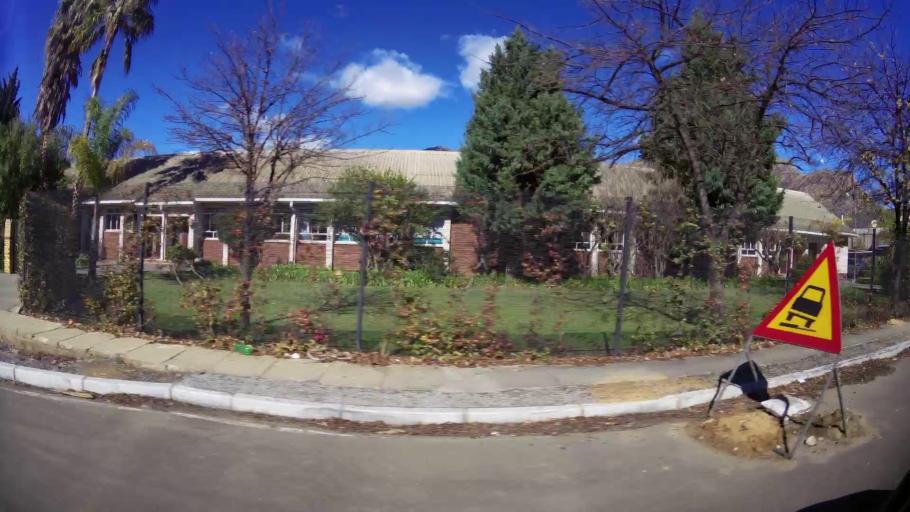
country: ZA
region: Western Cape
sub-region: Cape Winelands District Municipality
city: Ashton
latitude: -33.7885
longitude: 20.1246
